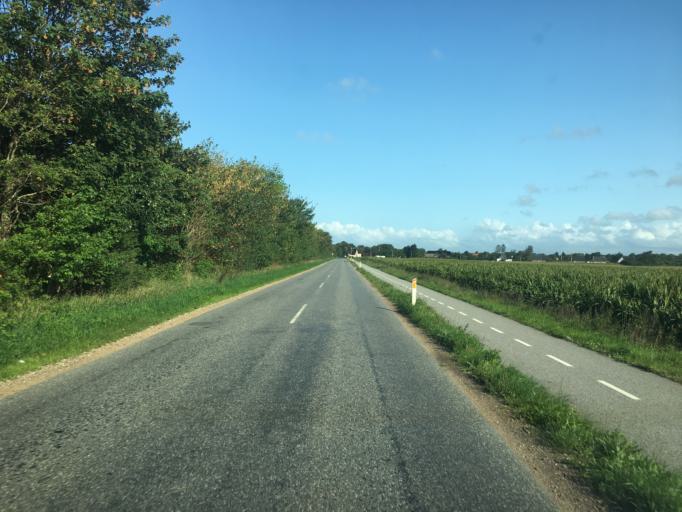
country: DK
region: South Denmark
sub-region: Tonder Kommune
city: Sherrebek
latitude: 55.1458
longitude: 8.7574
